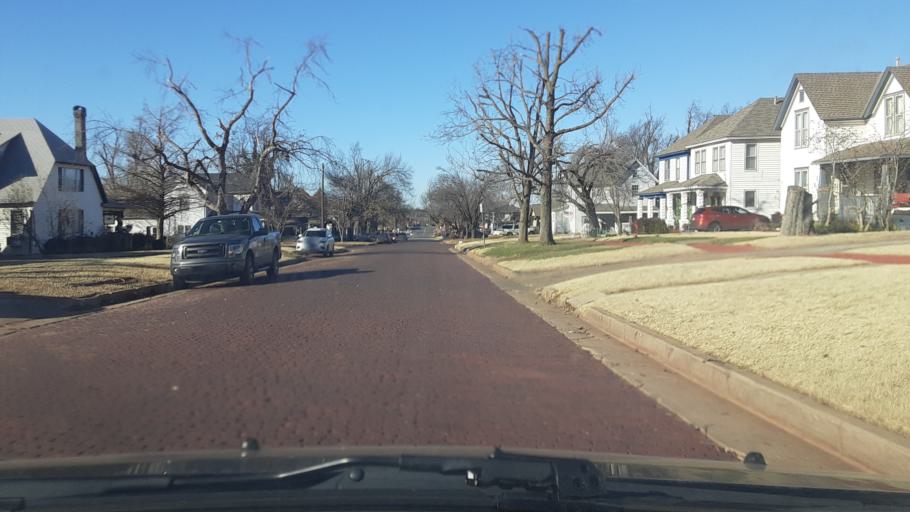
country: US
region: Oklahoma
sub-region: Logan County
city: Guthrie
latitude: 35.8791
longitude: -97.4194
